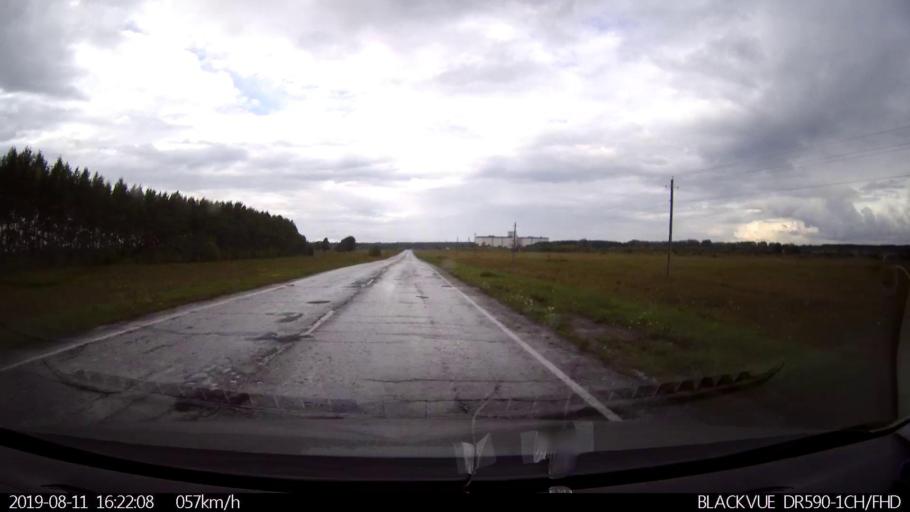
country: RU
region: Ulyanovsk
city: Mayna
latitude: 54.0854
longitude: 47.5945
